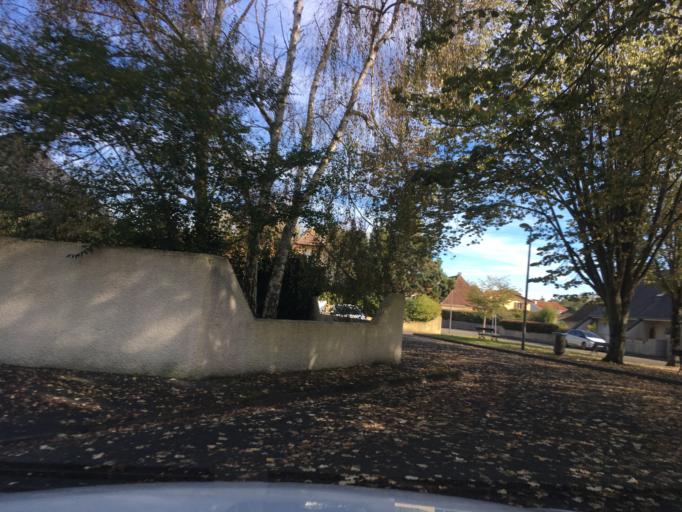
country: FR
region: Aquitaine
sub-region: Departement des Pyrenees-Atlantiques
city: Lons
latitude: 43.3336
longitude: -0.3773
